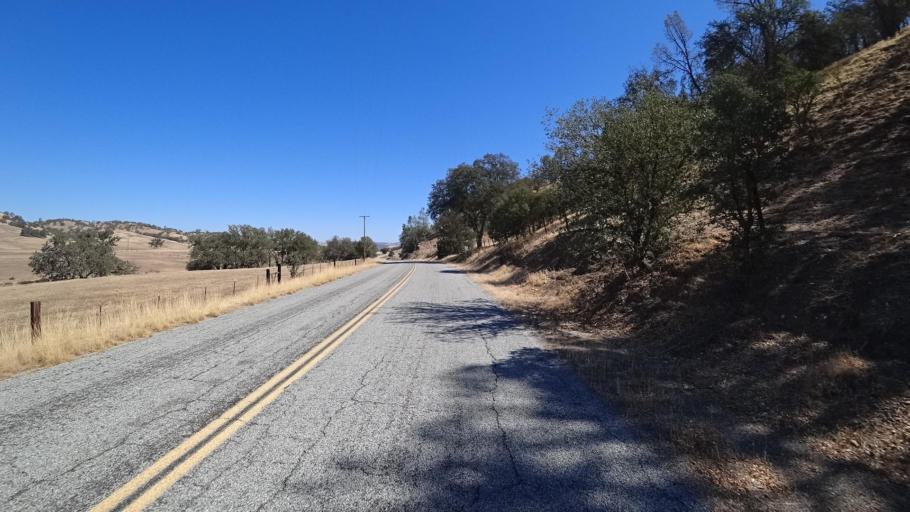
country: US
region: California
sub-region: San Luis Obispo County
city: San Miguel
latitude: 35.8256
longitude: -120.6475
